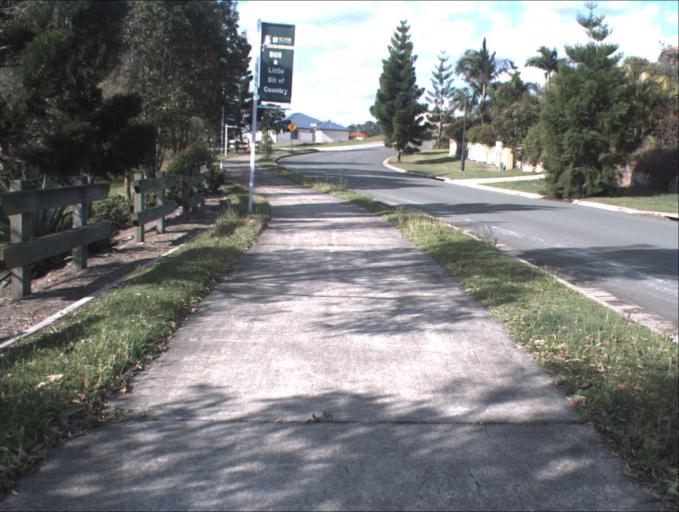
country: AU
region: Queensland
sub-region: Logan
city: Chambers Flat
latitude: -27.7715
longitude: 153.1014
